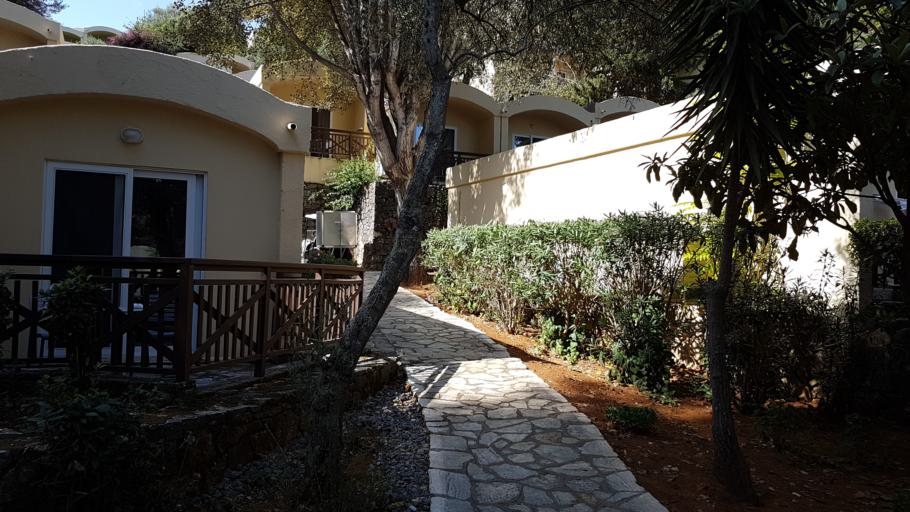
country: GR
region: Ionian Islands
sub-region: Nomos Kerkyras
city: Kontokali
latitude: 39.6670
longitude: 19.8510
